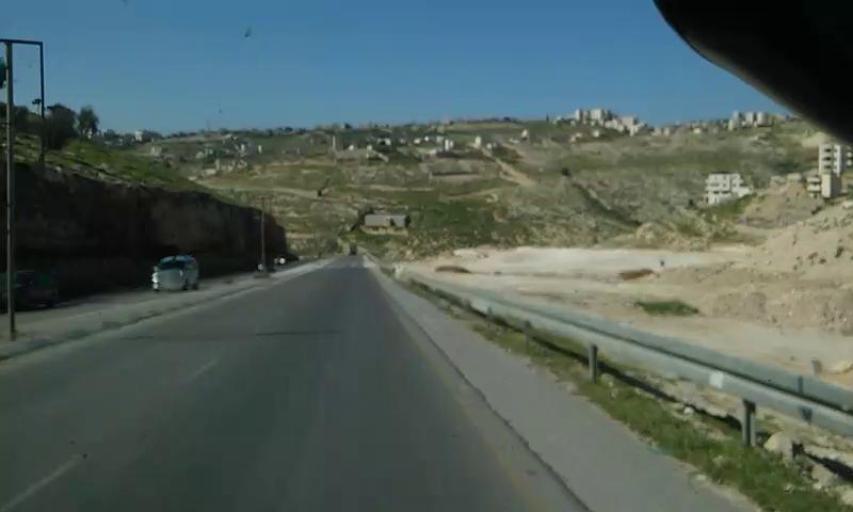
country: PS
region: West Bank
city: Abu Dis
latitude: 31.7521
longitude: 35.2784
